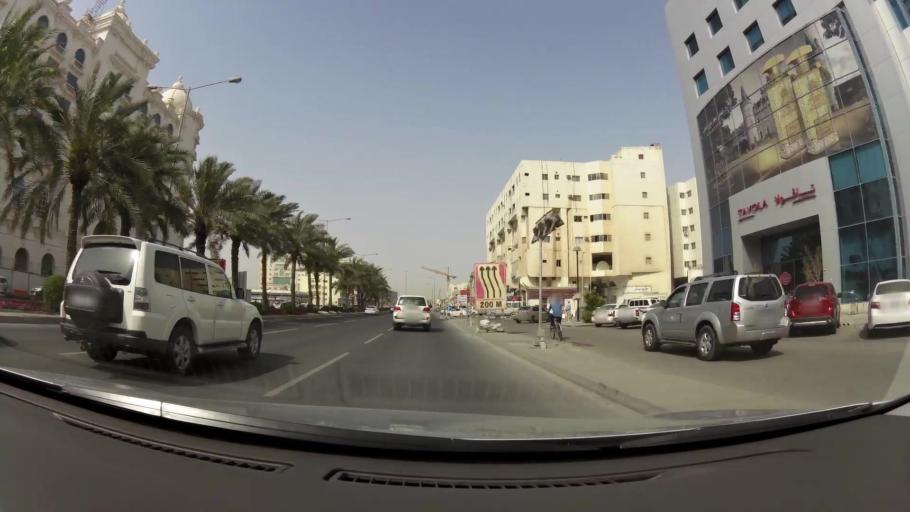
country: QA
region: Baladiyat ad Dawhah
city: Doha
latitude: 25.2811
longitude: 51.5012
